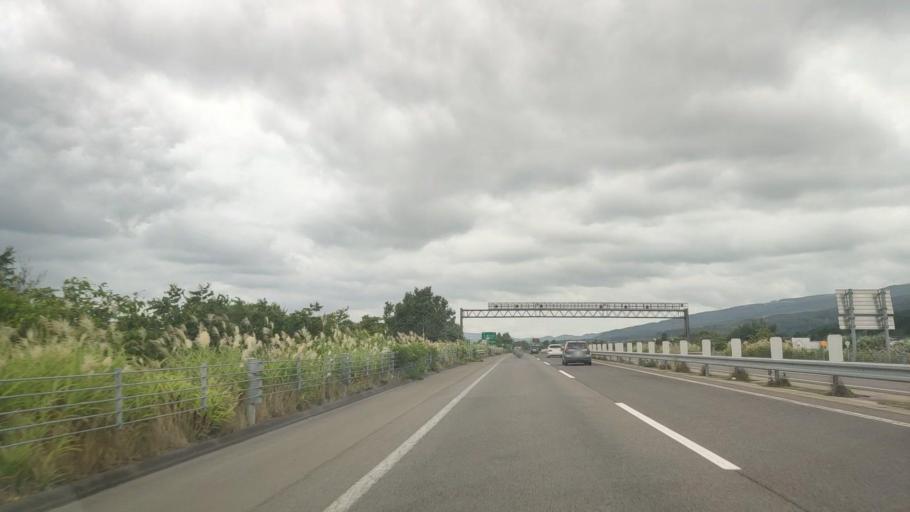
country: JP
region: Hokkaido
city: Nanae
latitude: 41.8603
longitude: 140.7338
